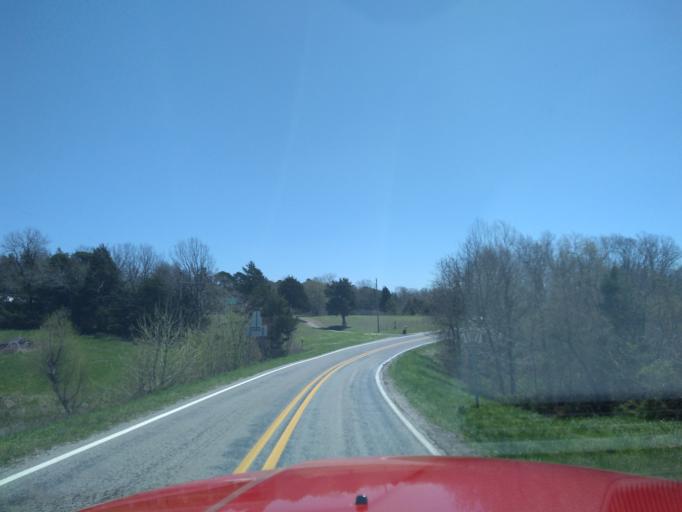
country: US
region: Arkansas
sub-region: Washington County
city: West Fork
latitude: 35.8434
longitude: -94.2736
